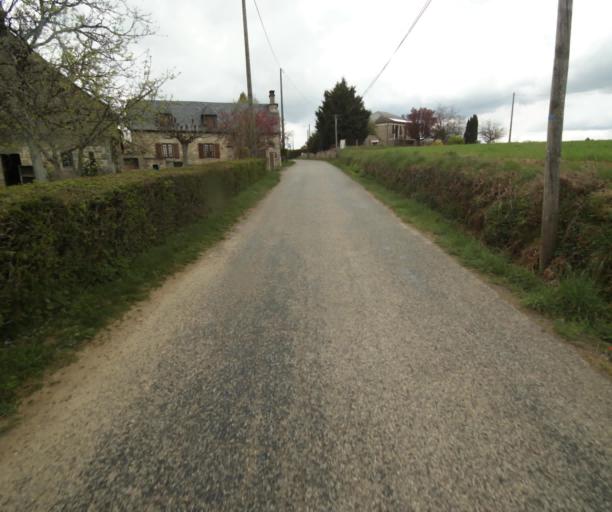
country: FR
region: Limousin
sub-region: Departement de la Correze
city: Laguenne
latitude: 45.2510
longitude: 1.8634
